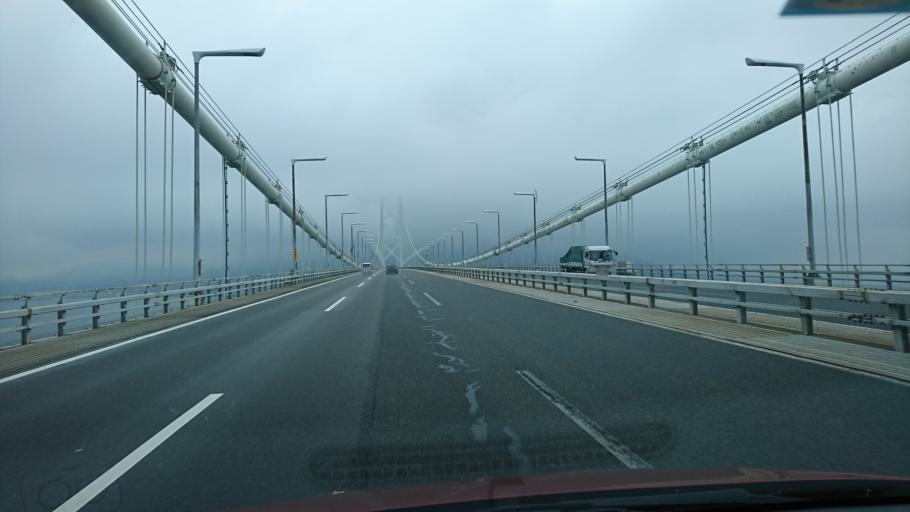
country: JP
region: Hyogo
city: Akashi
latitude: 34.6185
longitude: 135.0226
